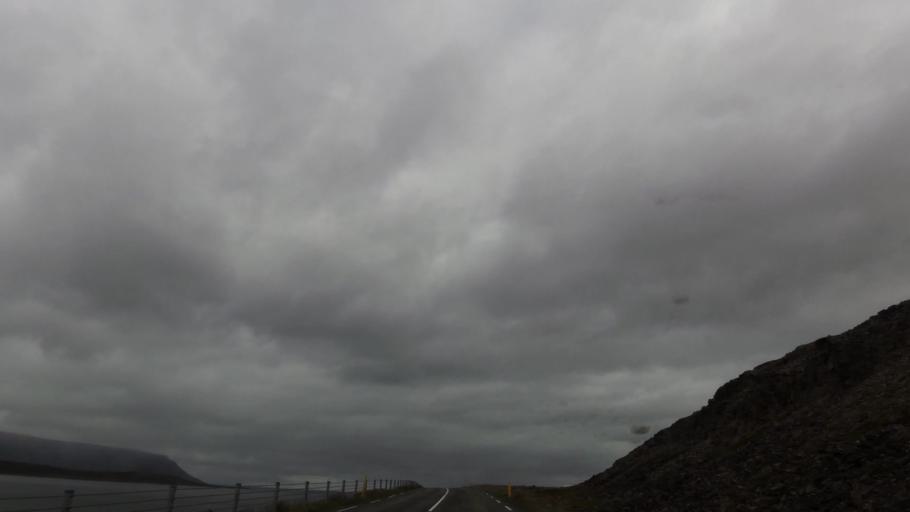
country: IS
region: Westfjords
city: Isafjoerdur
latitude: 65.9995
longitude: -22.7818
